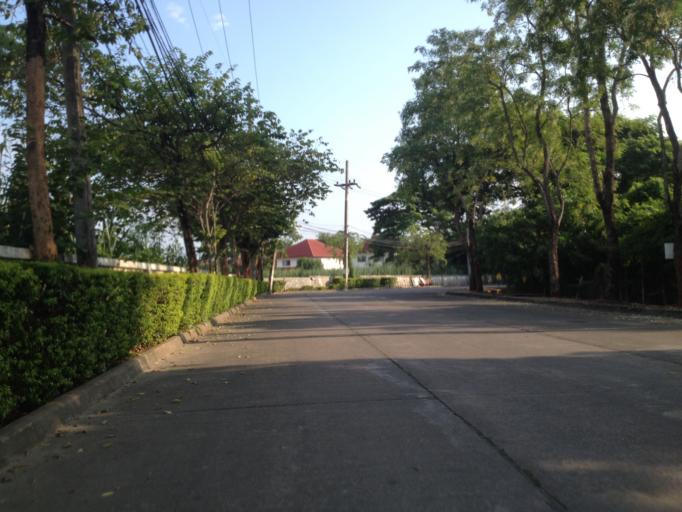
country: TH
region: Chiang Mai
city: Hang Dong
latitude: 18.7434
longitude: 98.9413
